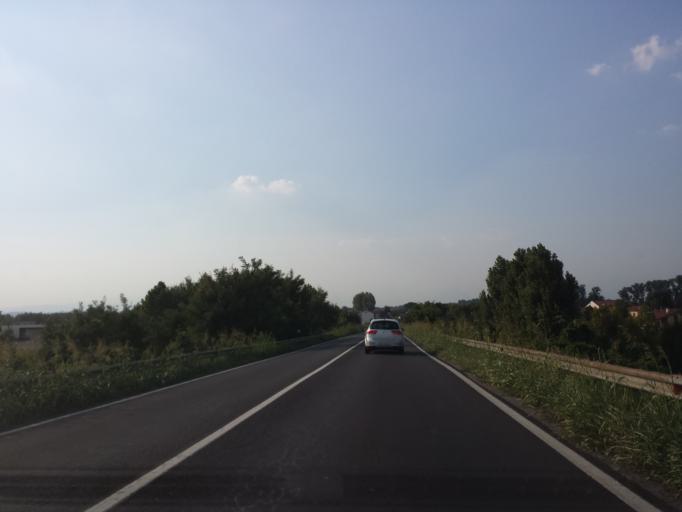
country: IT
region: Veneto
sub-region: Provincia di Vicenza
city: Grisignano di Zocco
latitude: 45.4834
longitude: 11.6807
